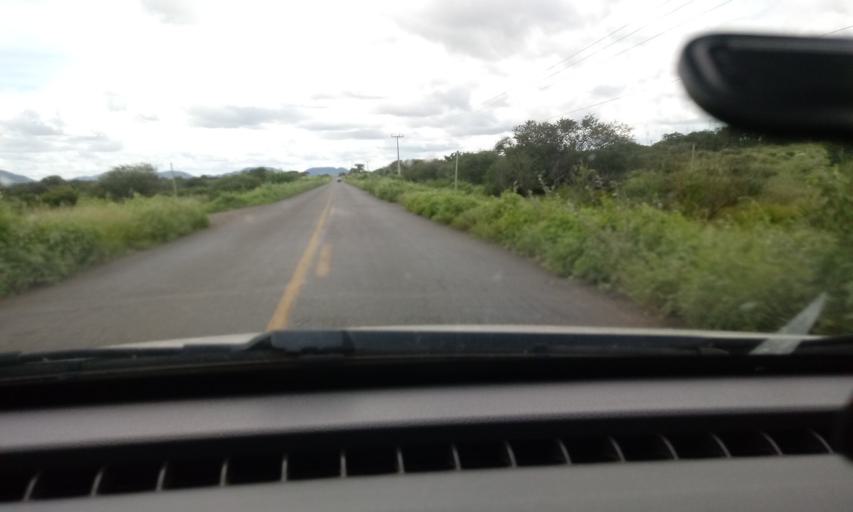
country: BR
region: Bahia
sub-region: Guanambi
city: Guanambi
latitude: -14.1094
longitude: -42.8656
